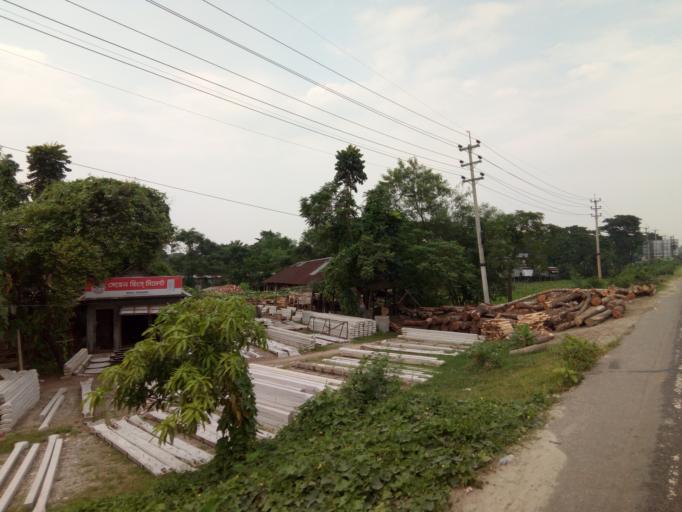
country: BD
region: Dhaka
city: Dohar
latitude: 23.5415
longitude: 90.2949
